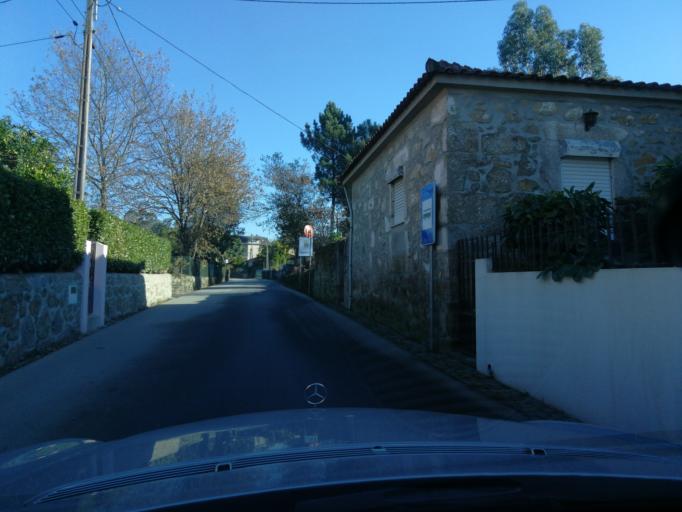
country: PT
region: Braga
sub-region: Braga
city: Adaufe
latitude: 41.6151
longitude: -8.4063
